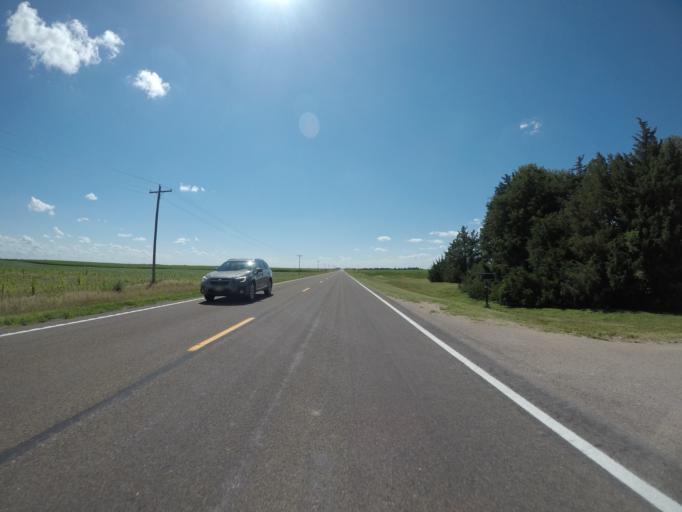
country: US
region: Nebraska
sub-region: Chase County
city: Imperial
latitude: 40.5377
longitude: -101.6774
